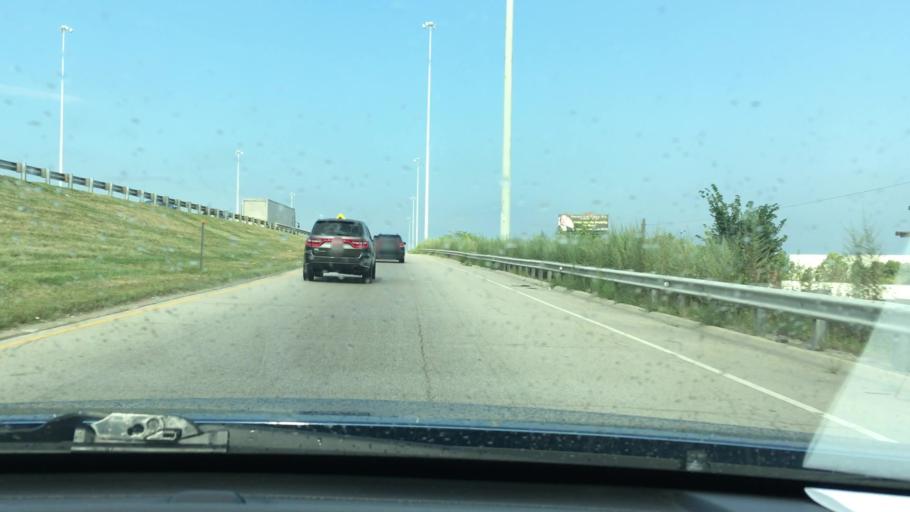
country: US
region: Illinois
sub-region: Cook County
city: Cicero
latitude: 41.8175
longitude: -87.7408
